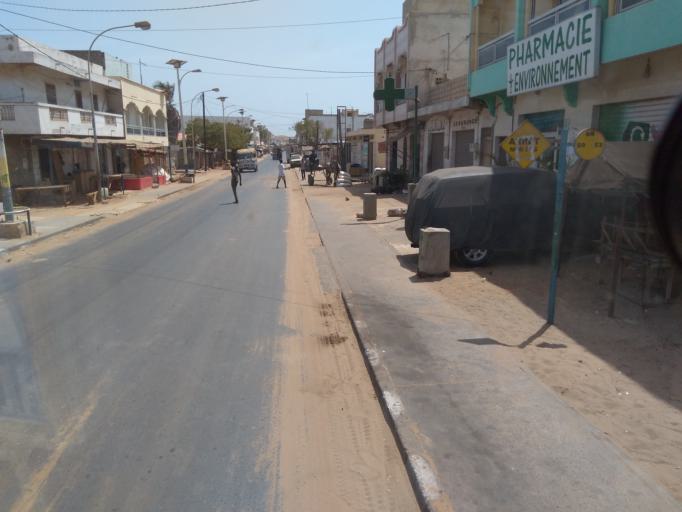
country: SN
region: Dakar
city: Pikine
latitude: 14.7904
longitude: -17.3421
